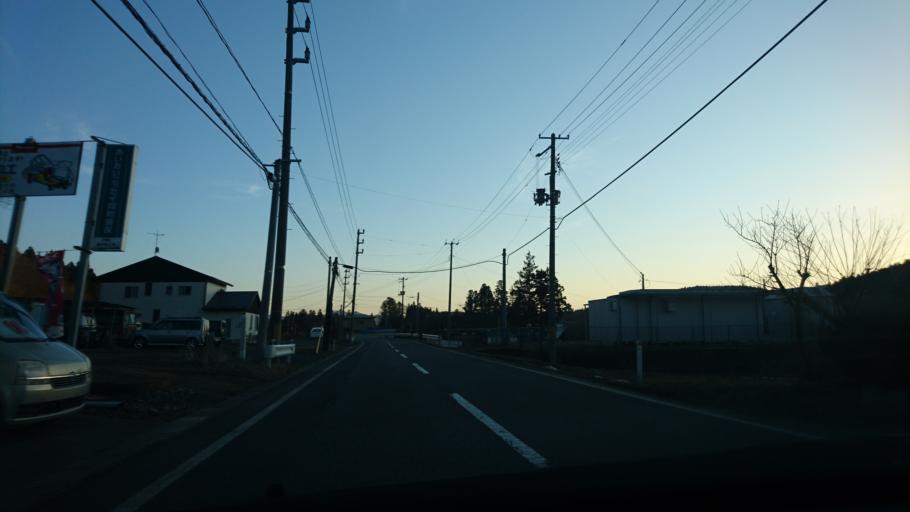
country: JP
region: Iwate
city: Mizusawa
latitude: 39.0304
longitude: 141.2948
